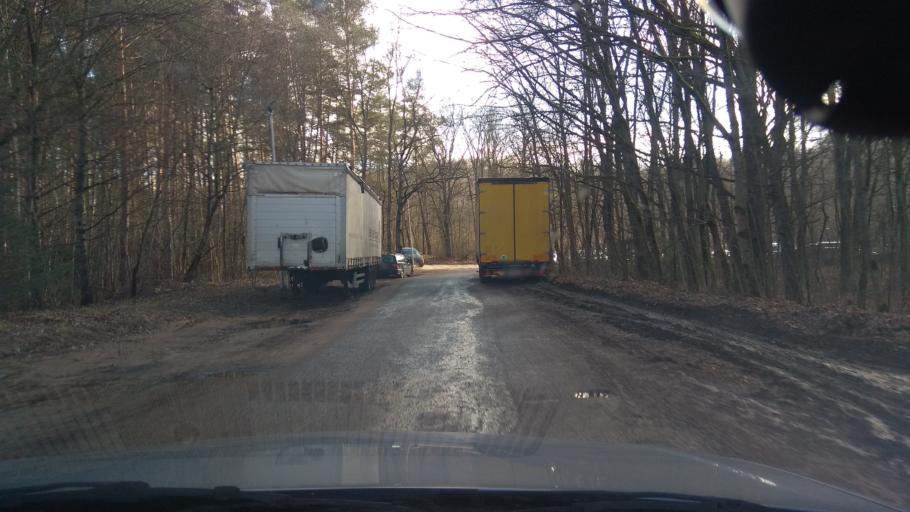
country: LT
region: Vilnius County
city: Lazdynai
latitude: 54.6422
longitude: 25.2233
